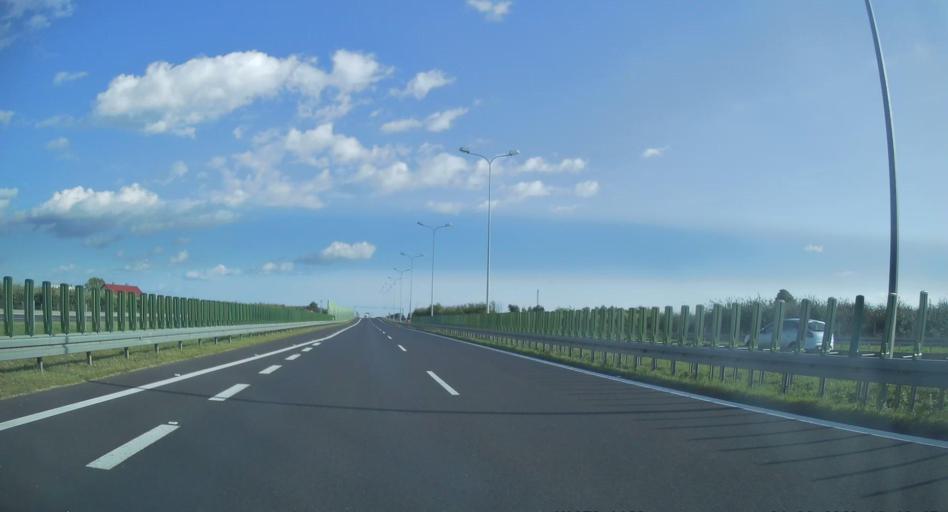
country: PL
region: Masovian Voivodeship
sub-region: Powiat grojecki
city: Goszczyn
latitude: 51.7581
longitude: 20.9051
